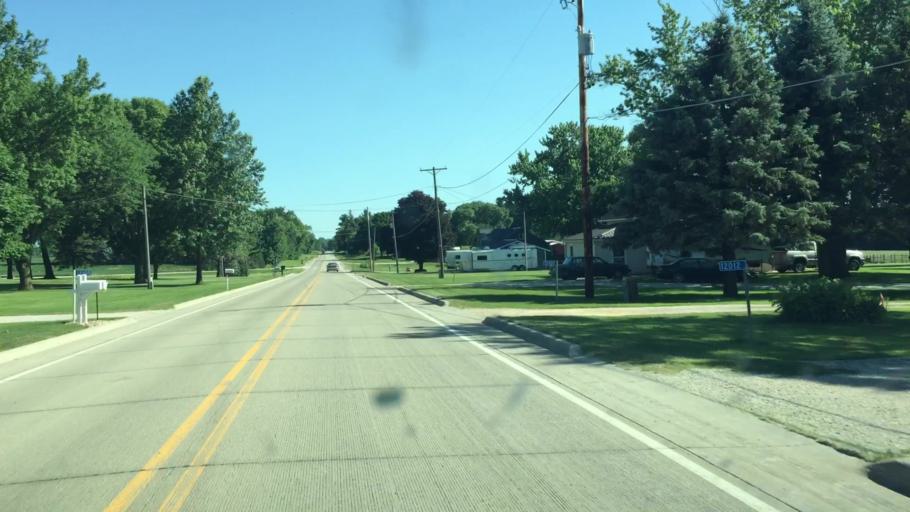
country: US
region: Iowa
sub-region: Linn County
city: Ely
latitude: 41.8641
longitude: -91.6464
